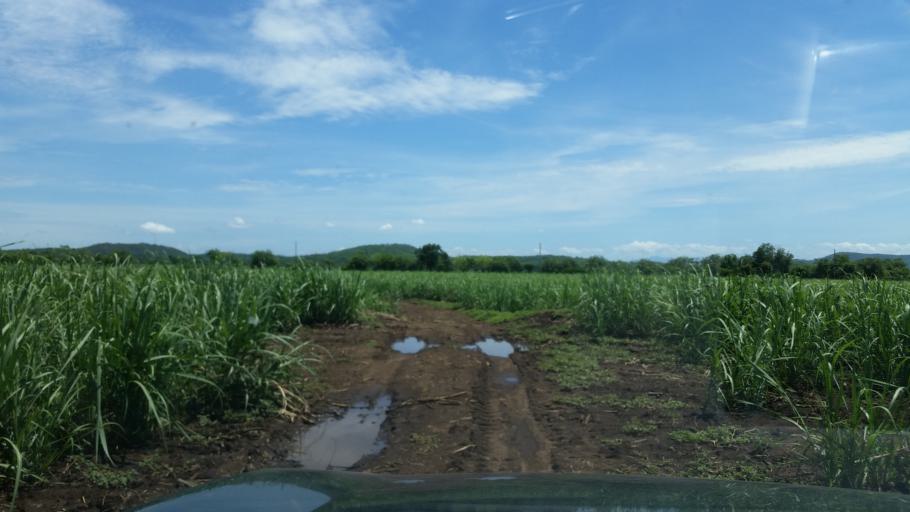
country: NI
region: Chinandega
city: Puerto Morazan
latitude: 12.7712
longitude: -87.1212
